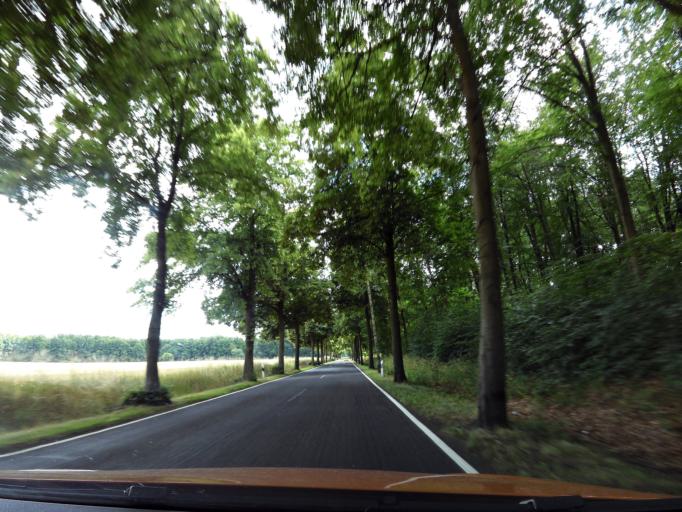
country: DE
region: Brandenburg
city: Rangsdorf
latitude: 52.3155
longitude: 13.4570
